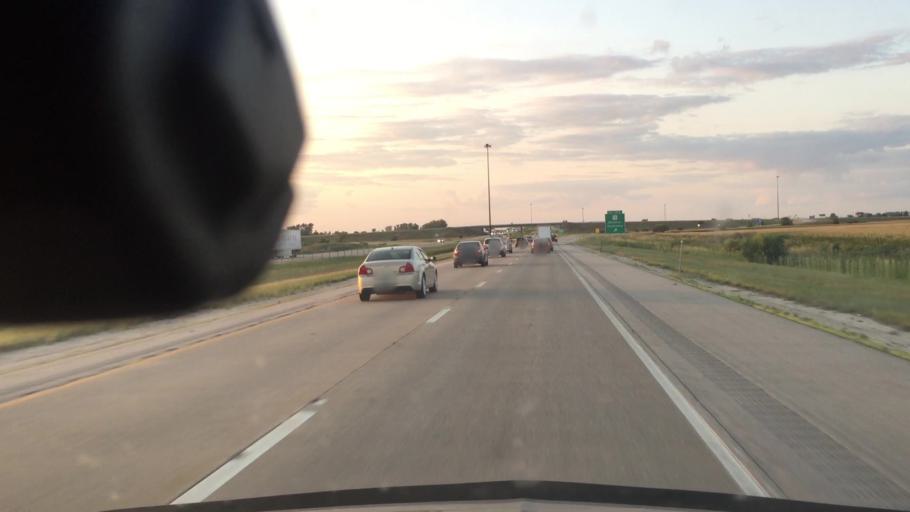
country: US
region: Illinois
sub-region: Livingston County
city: Dwight
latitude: 41.0872
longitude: -88.4512
